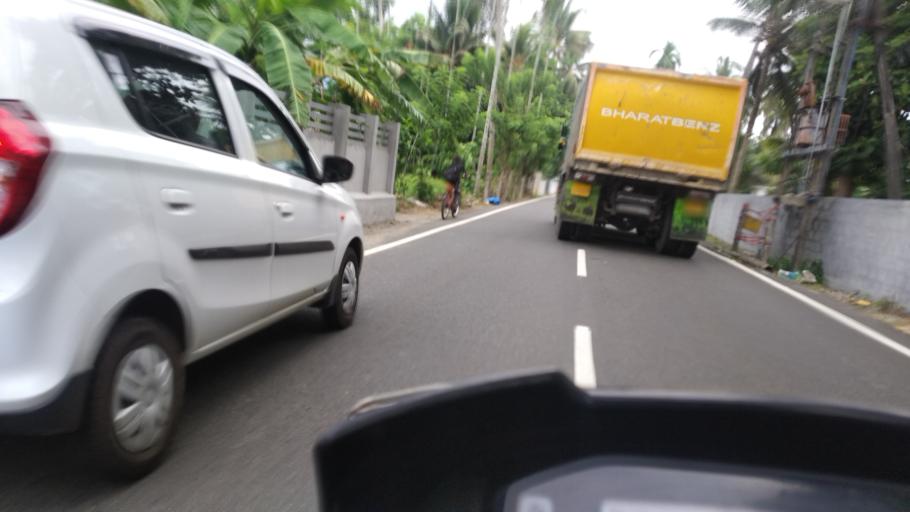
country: IN
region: Kerala
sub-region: Ernakulam
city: Elur
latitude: 10.1545
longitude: 76.2762
